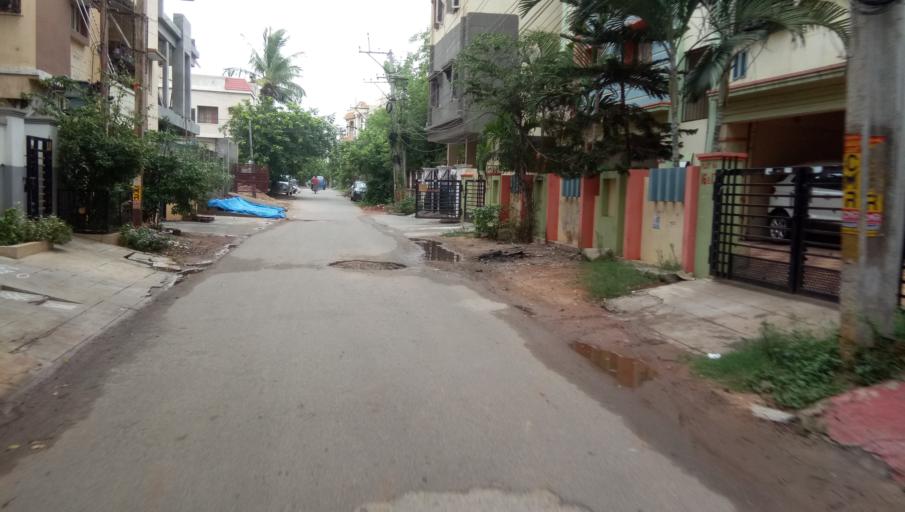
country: IN
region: Telangana
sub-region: Rangareddi
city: Lal Bahadur Nagar
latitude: 17.3578
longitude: 78.5430
